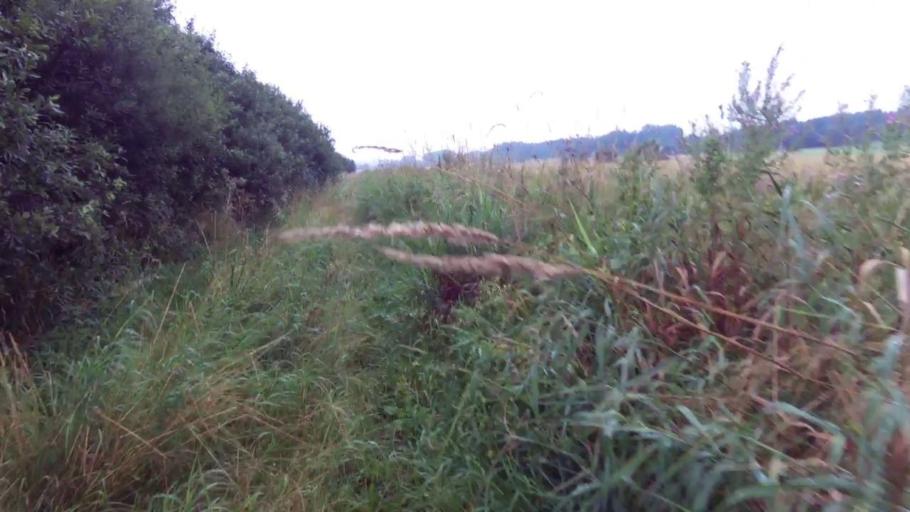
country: PL
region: West Pomeranian Voivodeship
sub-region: Powiat choszczenski
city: Choszczno
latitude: 53.2503
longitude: 15.4102
